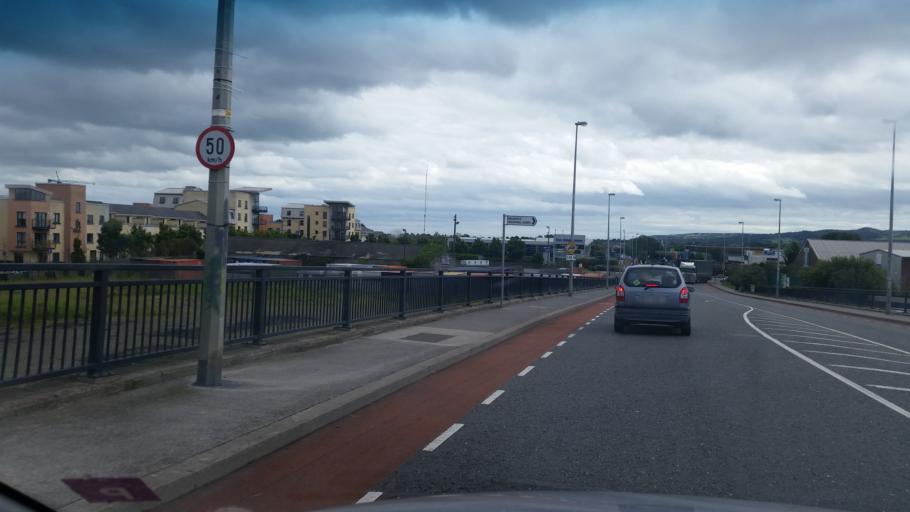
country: IE
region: Leinster
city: Donaghmede
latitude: 53.3979
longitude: -6.1496
